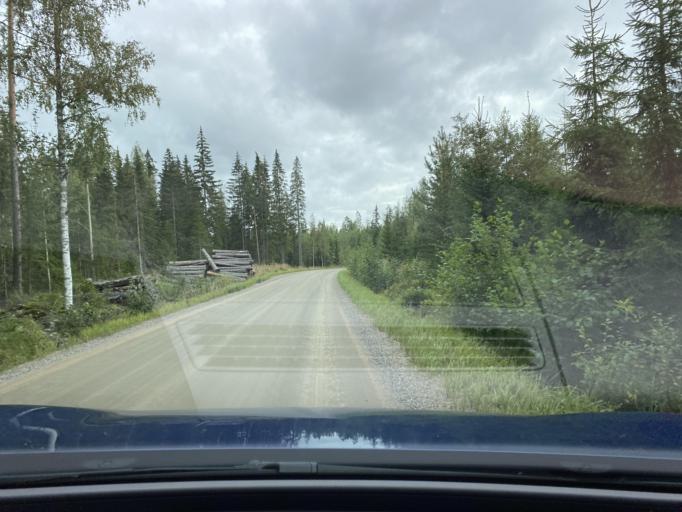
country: FI
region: Pirkanmaa
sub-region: Lounais-Pirkanmaa
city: Punkalaidun
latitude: 61.2098
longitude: 23.1750
